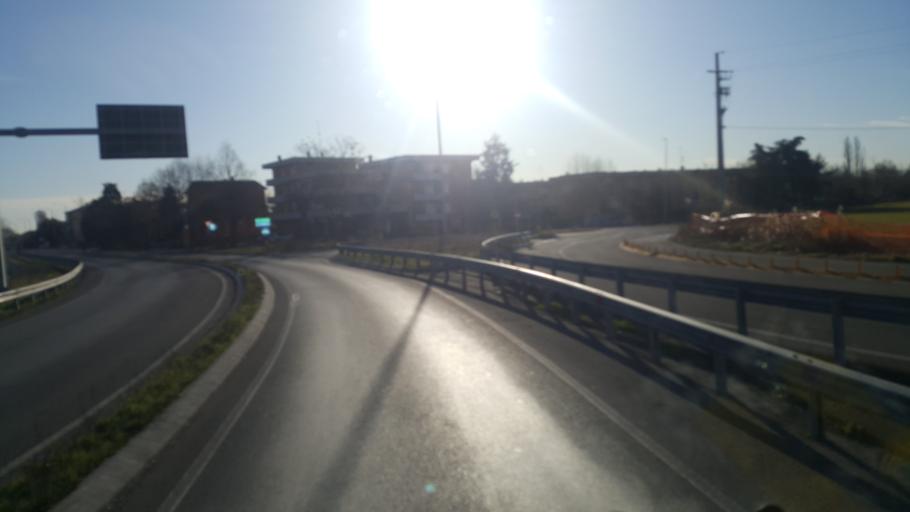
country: IT
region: Emilia-Romagna
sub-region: Provincia di Modena
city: Campogalliano
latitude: 44.6482
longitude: 10.8383
